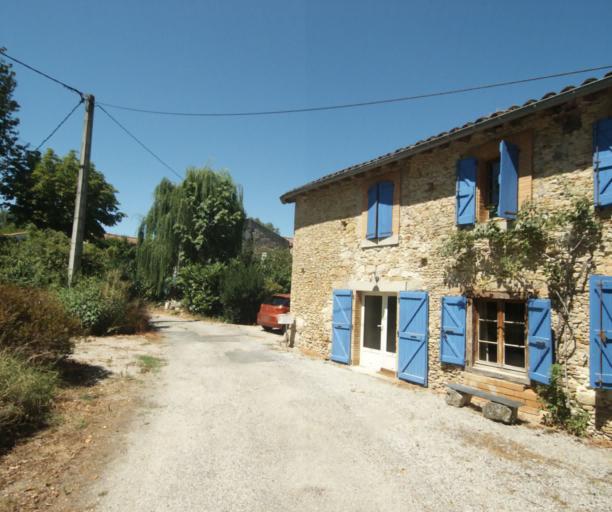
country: FR
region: Midi-Pyrenees
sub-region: Departement de la Haute-Garonne
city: Saint-Felix-Lauragais
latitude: 43.4808
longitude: 1.9285
